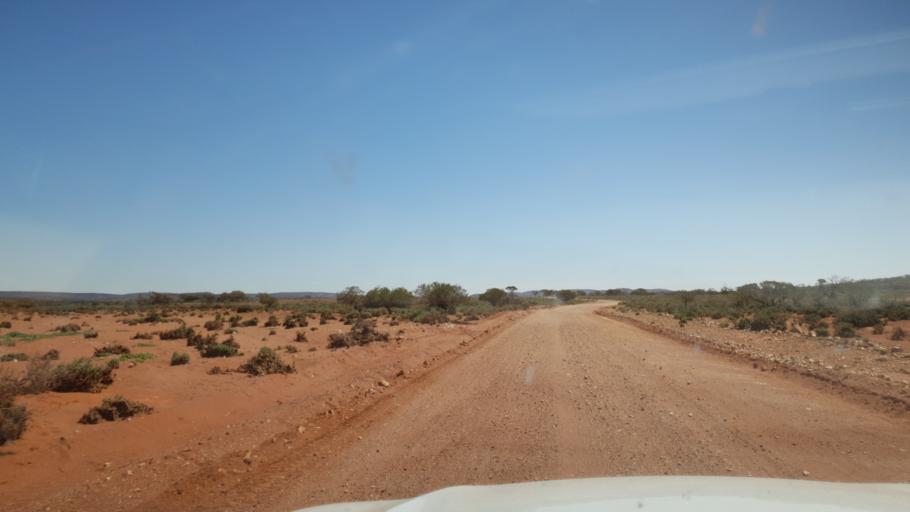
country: AU
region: South Australia
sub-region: Whyalla
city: Whyalla
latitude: -32.6233
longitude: 136.7978
